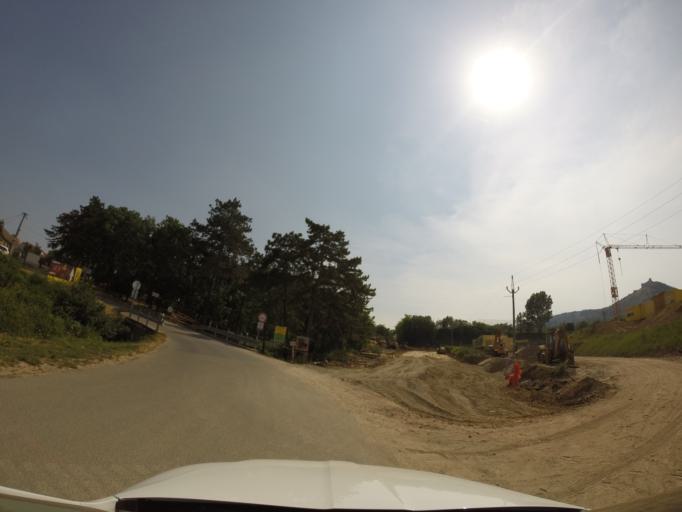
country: CZ
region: South Moravian
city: Sakvice
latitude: 48.8778
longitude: 16.6760
